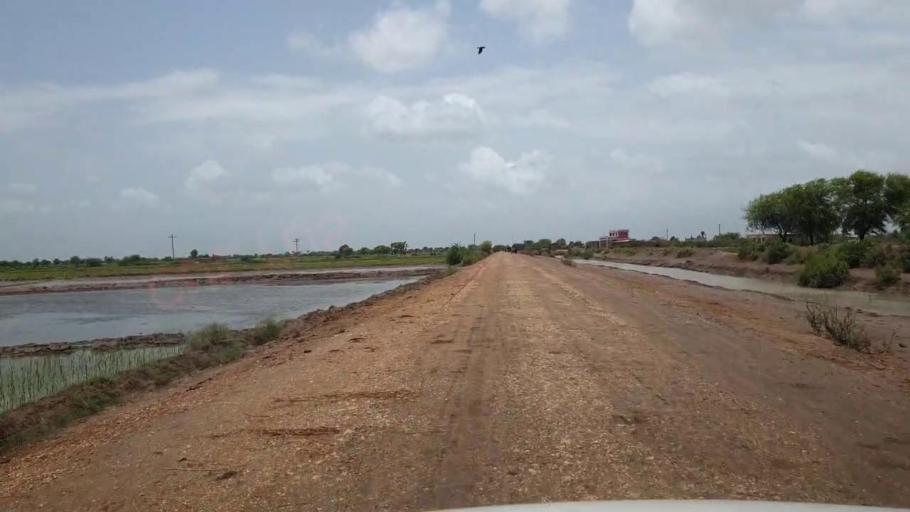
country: PK
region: Sindh
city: Kario
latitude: 24.7150
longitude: 68.5865
